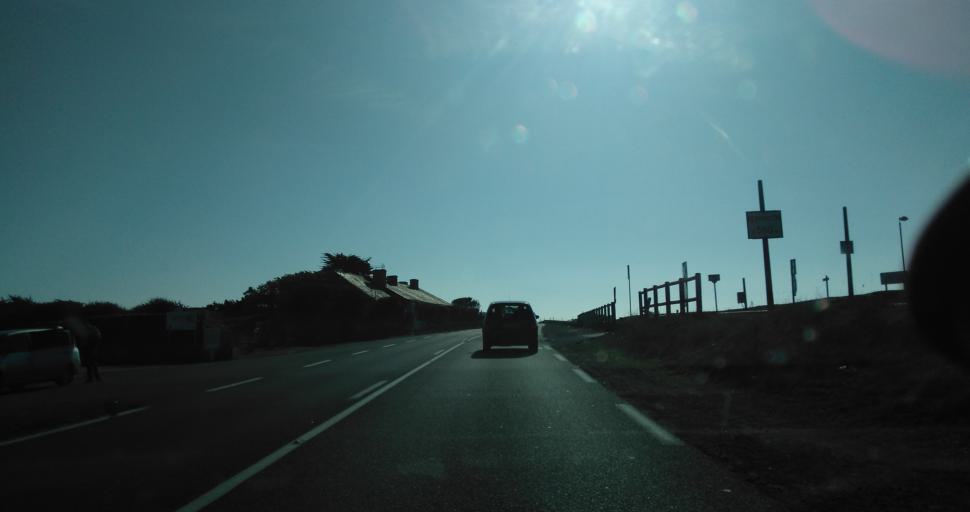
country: FR
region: Brittany
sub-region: Departement du Morbihan
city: Saint-Pierre-Quiberon
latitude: 47.5430
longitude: -3.1345
